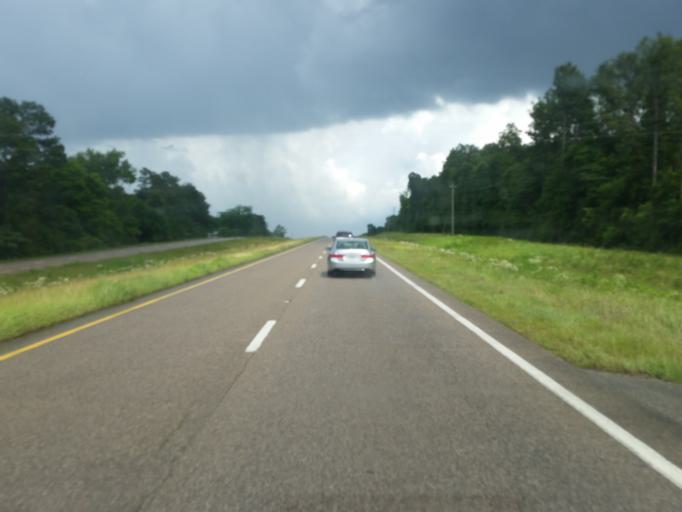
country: US
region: Mississippi
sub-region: George County
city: Lucedale
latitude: 30.9155
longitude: -88.4936
